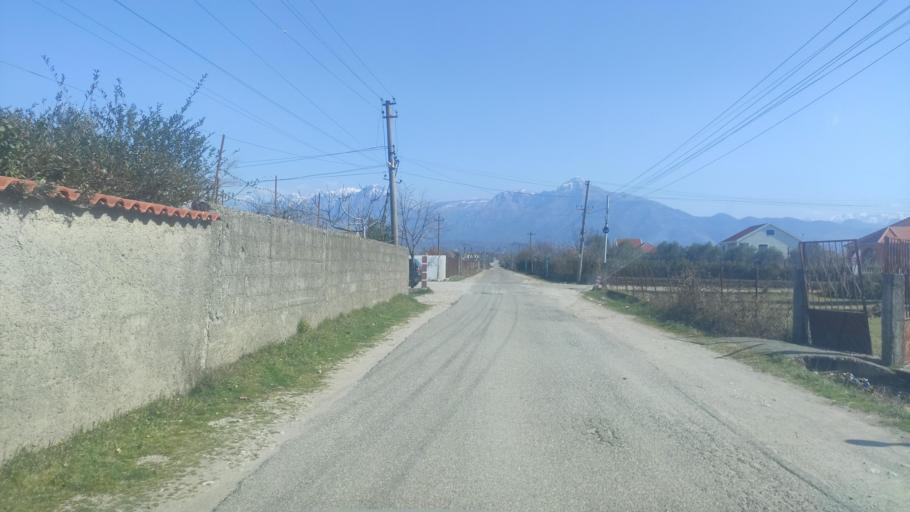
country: AL
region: Shkoder
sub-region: Rrethi i Malesia e Madhe
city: Grude-Fushe
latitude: 42.1622
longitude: 19.4604
